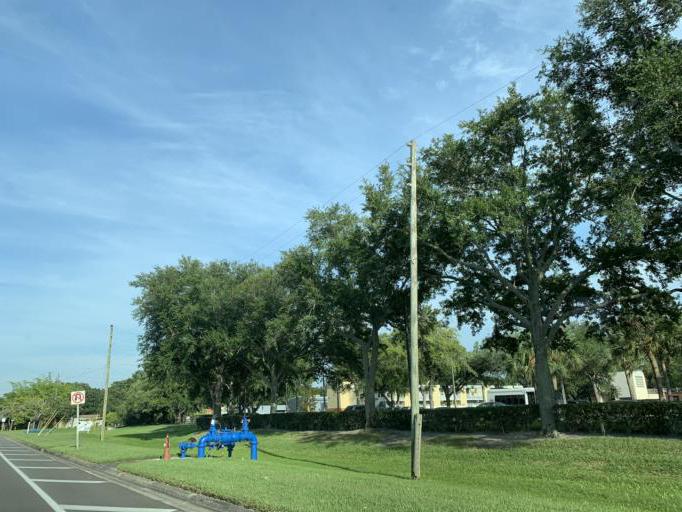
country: US
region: Florida
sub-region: Pinellas County
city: Lealman
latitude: 27.8031
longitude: -82.6333
